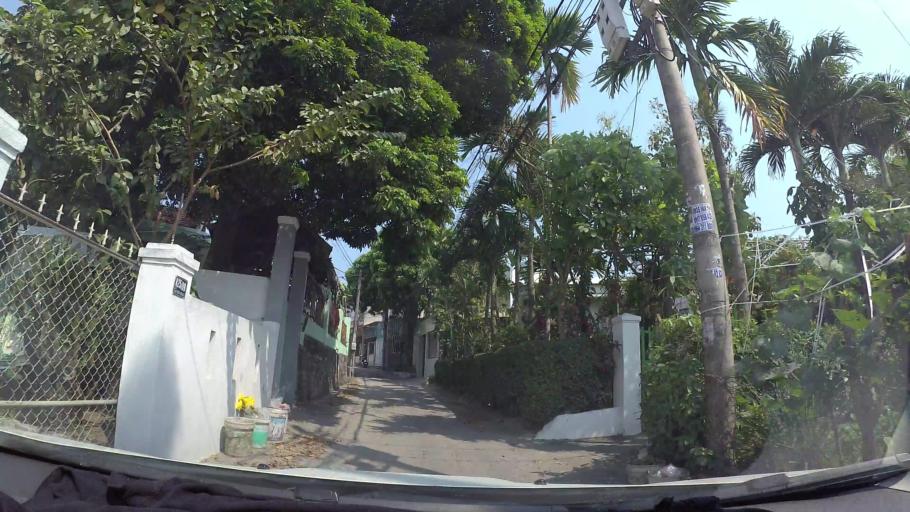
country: VN
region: Da Nang
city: Cam Le
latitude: 16.0123
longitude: 108.1993
